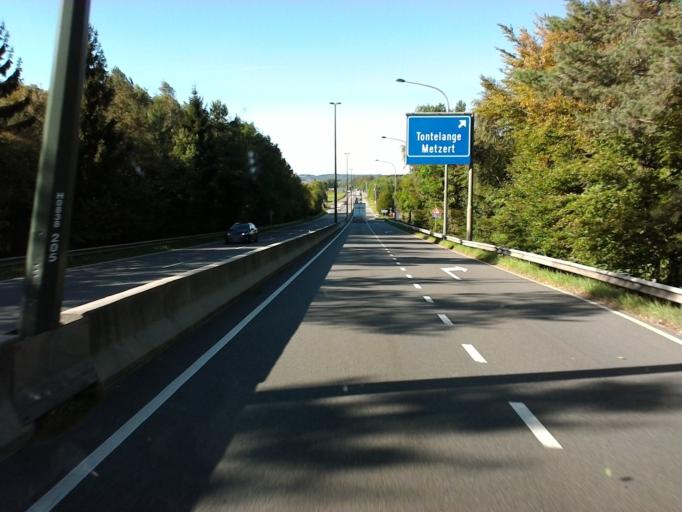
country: BE
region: Wallonia
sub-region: Province du Luxembourg
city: Attert
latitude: 49.7211
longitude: 5.7993
